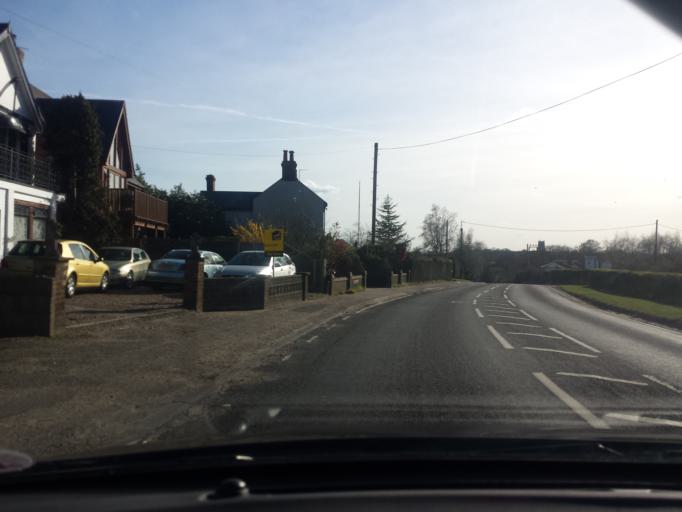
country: GB
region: England
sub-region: Essex
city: Brightlingsea
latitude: 51.8345
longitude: 1.0240
